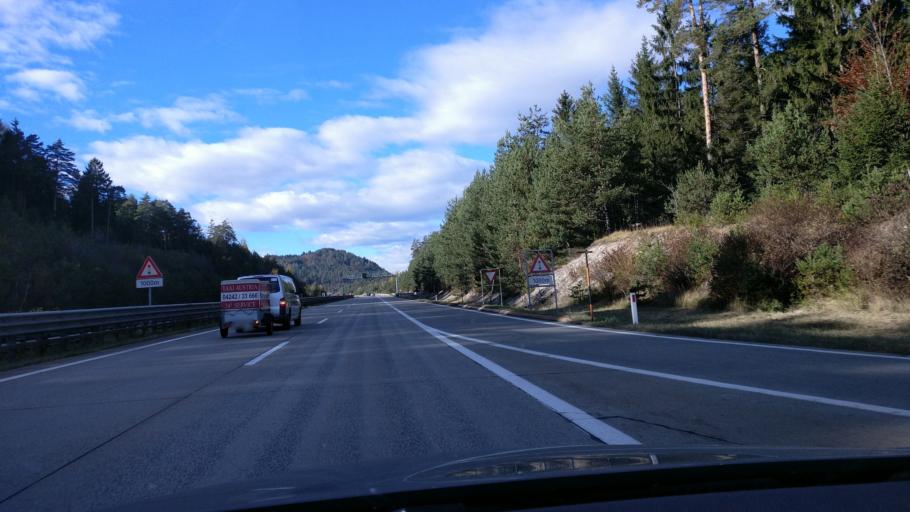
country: AT
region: Carinthia
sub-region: Politischer Bezirk Villach Land
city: Fresach
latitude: 46.6549
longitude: 13.7384
